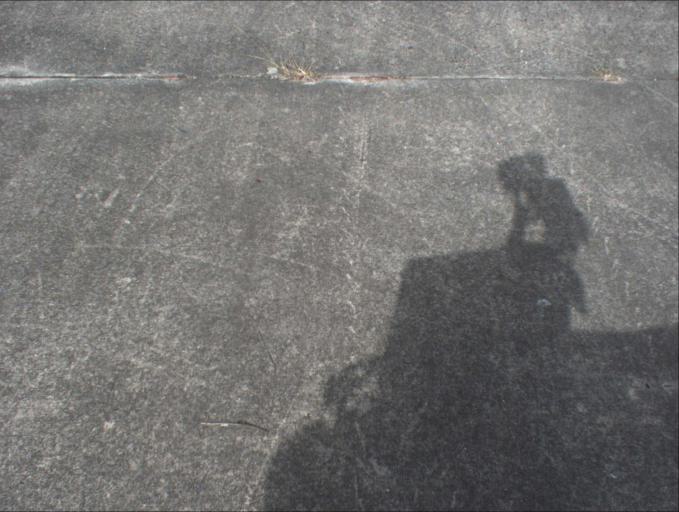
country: AU
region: Queensland
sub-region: Logan
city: Woodridge
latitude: -27.6425
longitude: 153.1005
